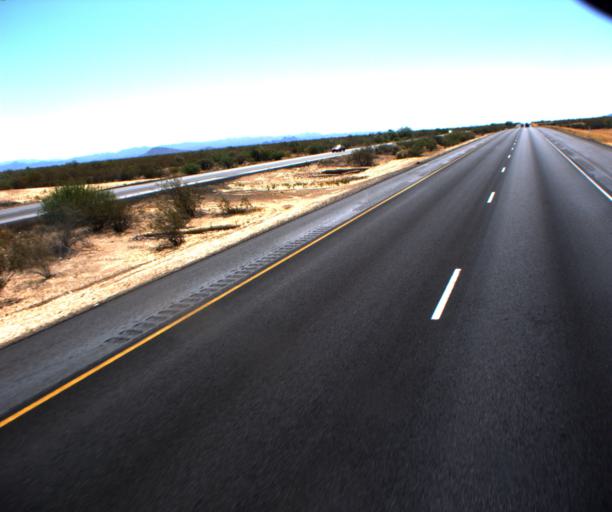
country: US
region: Arizona
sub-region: Yavapai County
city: Congress
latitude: 34.0776
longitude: -112.8853
